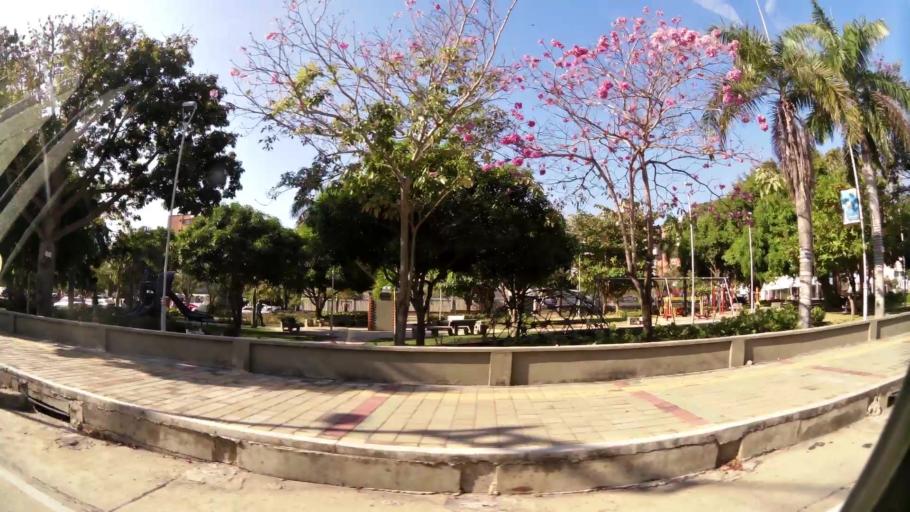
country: CO
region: Atlantico
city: Barranquilla
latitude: 11.0090
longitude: -74.8044
